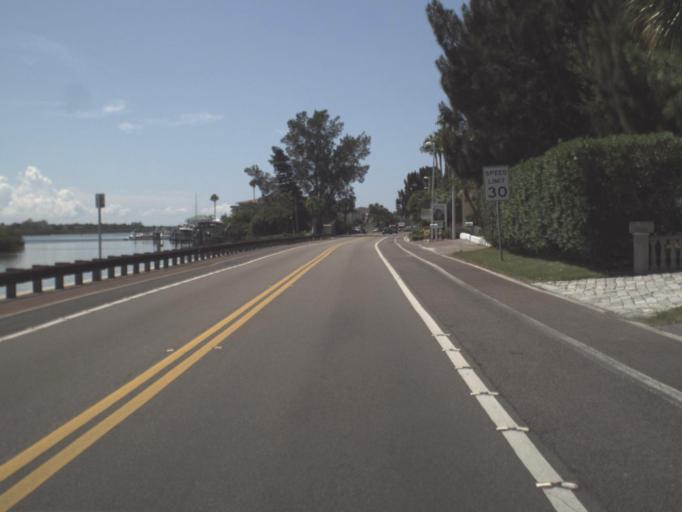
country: US
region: Florida
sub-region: Pinellas County
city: Indian Rocks Beach
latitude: 27.8699
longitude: -82.8496
